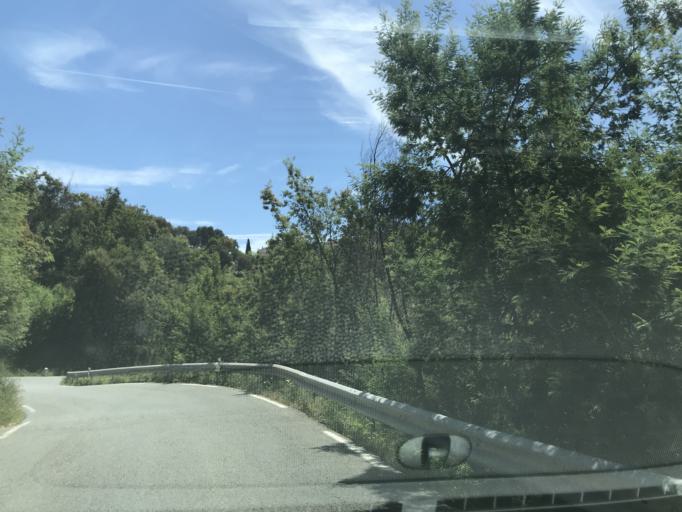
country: FR
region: Provence-Alpes-Cote d'Azur
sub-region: Departement des Alpes-Maritimes
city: Auribeau-sur-Siagne
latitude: 43.5862
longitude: 6.8975
